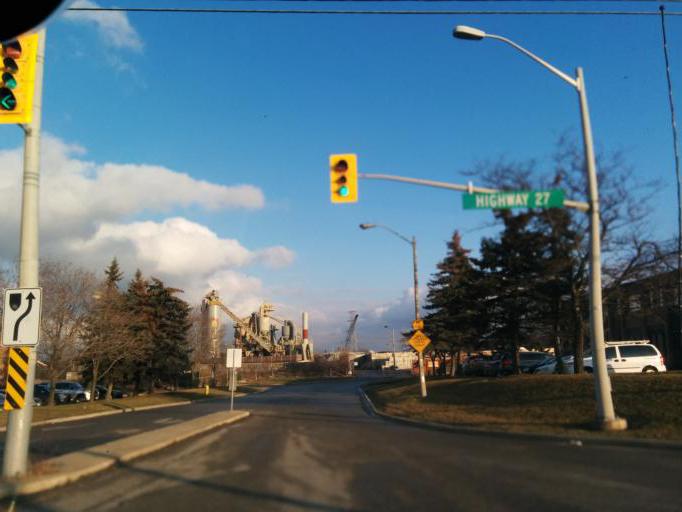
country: CA
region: Ontario
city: Etobicoke
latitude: 43.7773
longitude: -79.6224
